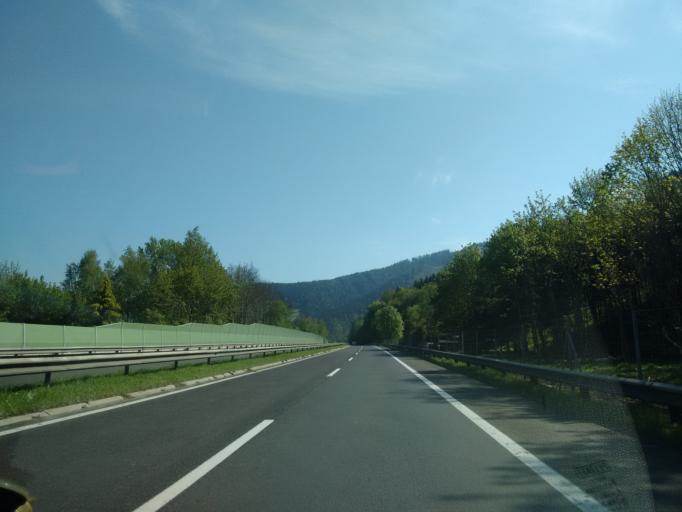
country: AT
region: Styria
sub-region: Politischer Bezirk Leoben
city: Leoben
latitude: 47.3558
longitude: 15.0990
